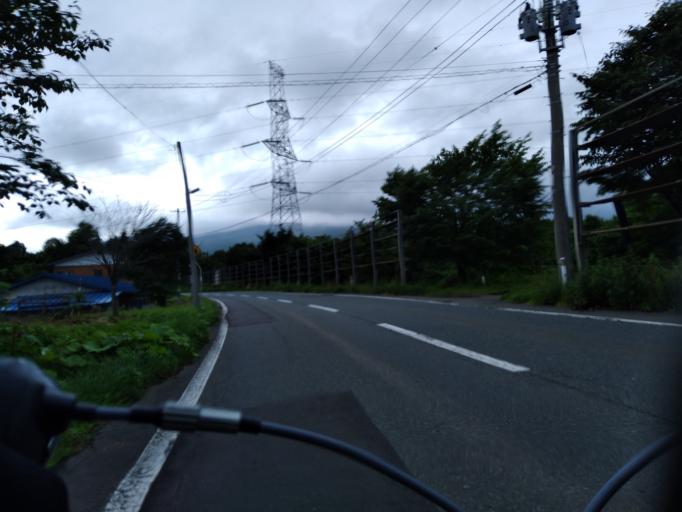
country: JP
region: Iwate
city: Morioka-shi
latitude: 39.8120
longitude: 141.0770
